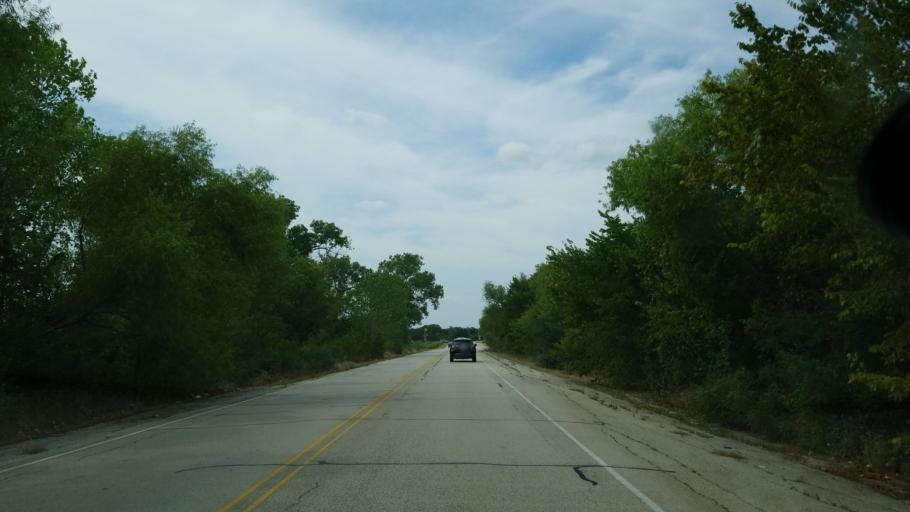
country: US
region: Texas
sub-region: Tarrant County
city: Hurst
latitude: 32.7993
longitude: -97.1413
